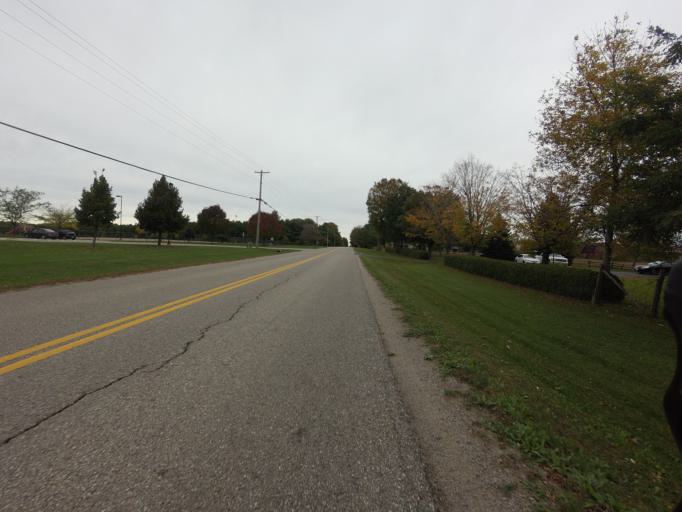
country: CA
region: Ontario
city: Brockville
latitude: 44.6657
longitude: -75.8770
